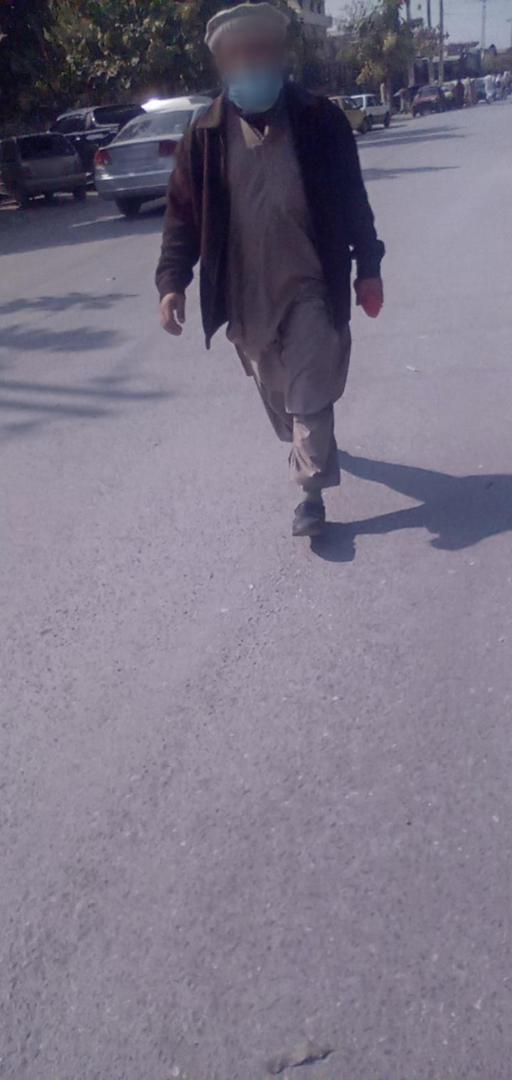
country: PK
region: Khyber Pakhtunkhwa
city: Peshawar
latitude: 33.9895
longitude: 71.4431
